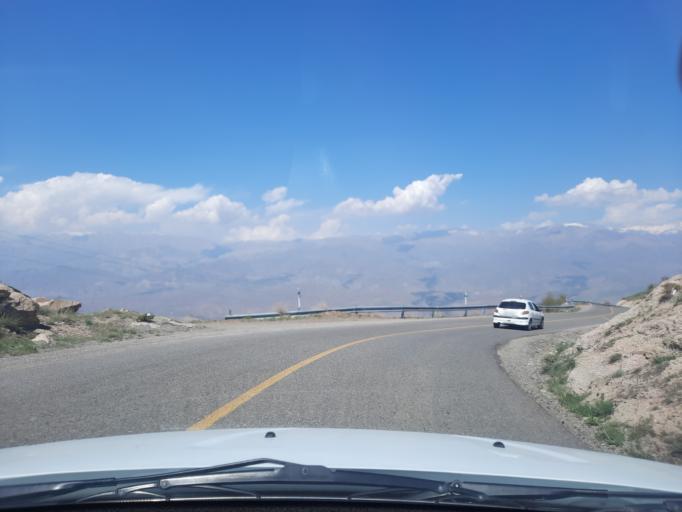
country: IR
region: Qazvin
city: Qazvin
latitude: 36.4110
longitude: 50.2347
